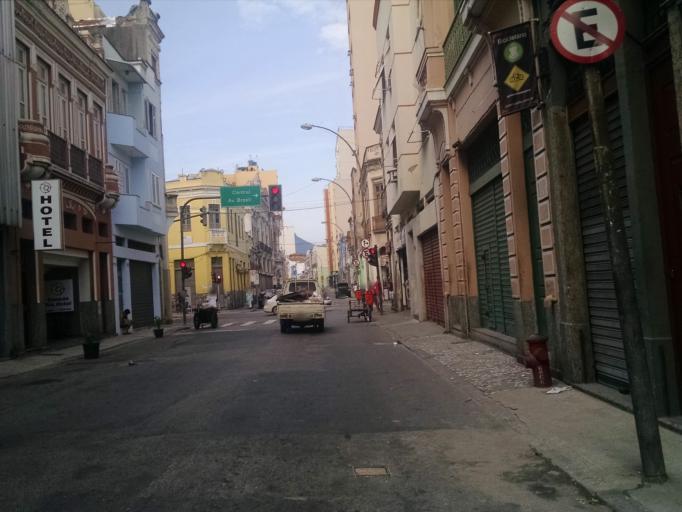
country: BR
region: Rio de Janeiro
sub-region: Rio De Janeiro
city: Rio de Janeiro
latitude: -22.9102
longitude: -43.1879
